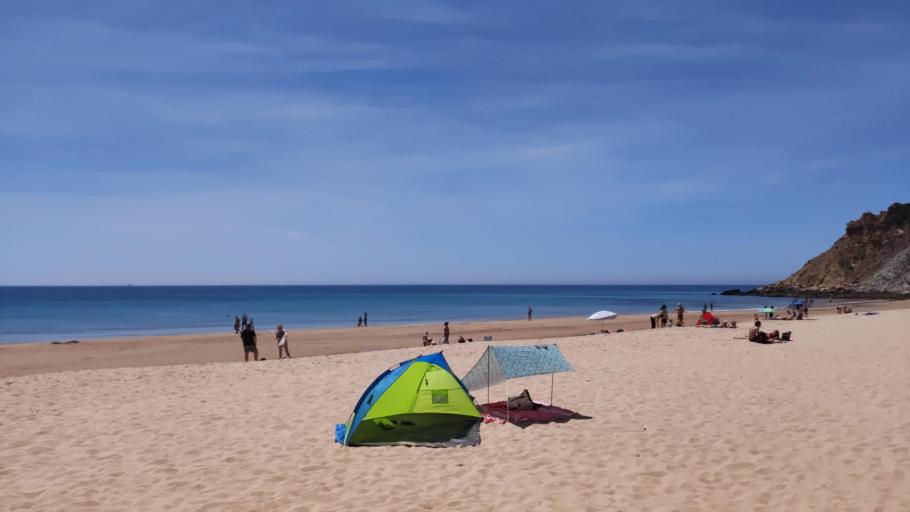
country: PT
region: Faro
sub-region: Lagos
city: Lagos
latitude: 37.0719
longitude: -8.7754
